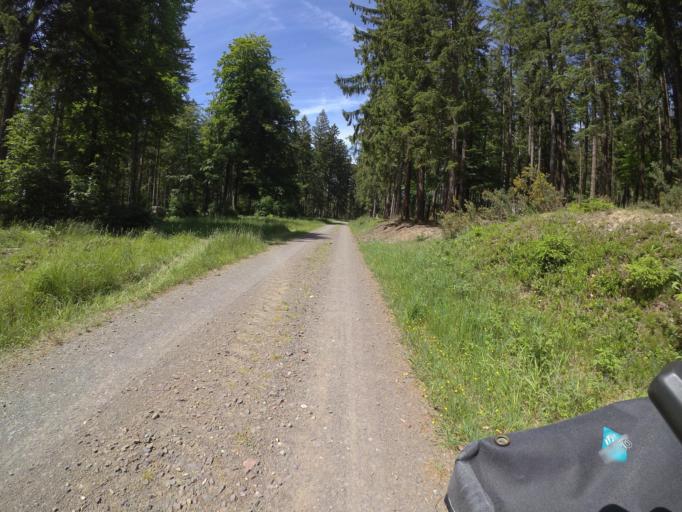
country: DE
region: Rheinland-Pfalz
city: Deuselbach
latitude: 49.7551
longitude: 7.0913
